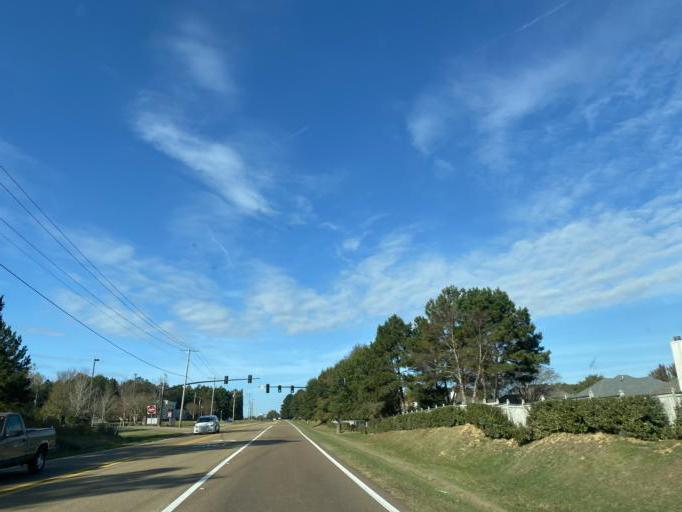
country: US
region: Mississippi
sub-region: Madison County
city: Madison
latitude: 32.4806
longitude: -90.1657
